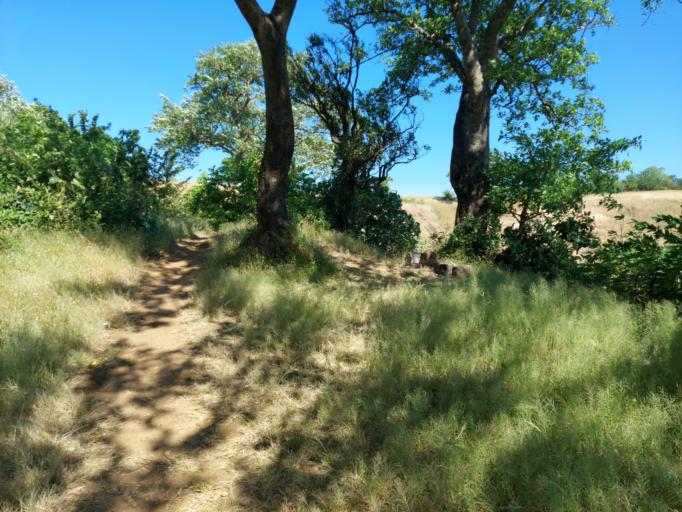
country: IN
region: Maharashtra
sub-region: Sindhudurg
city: Kudal
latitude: 16.0809
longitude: 73.8434
